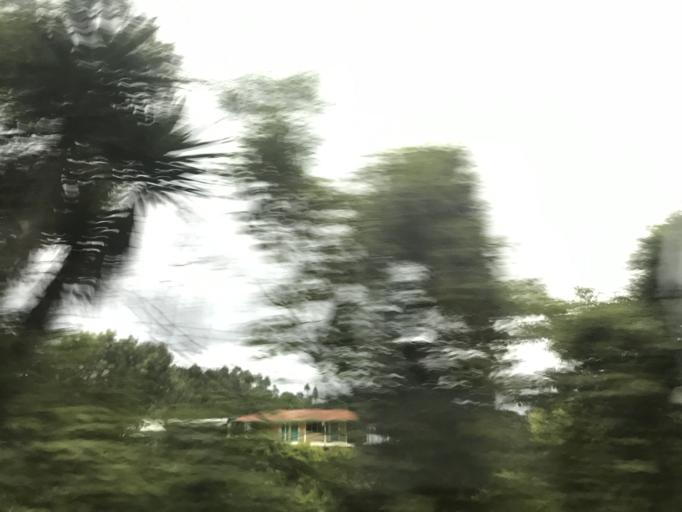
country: GT
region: Chimaltenango
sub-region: Municipio de Chimaltenango
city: Chimaltenango
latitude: 14.6699
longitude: -90.8506
